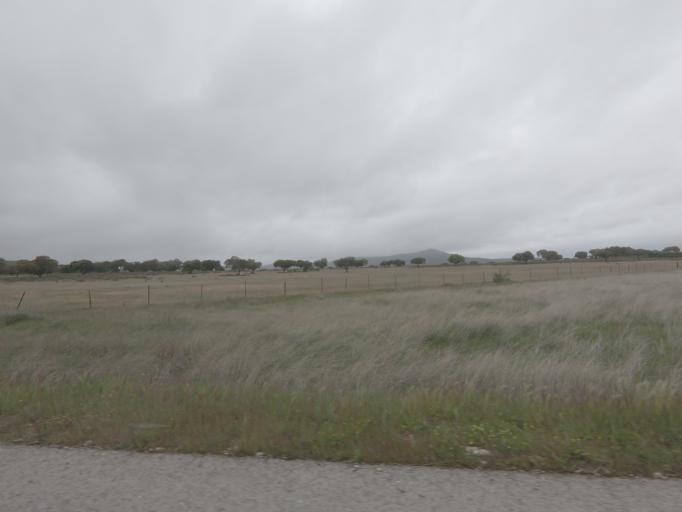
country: ES
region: Extremadura
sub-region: Provincia de Caceres
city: Malpartida de Caceres
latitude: 39.3128
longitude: -6.5092
